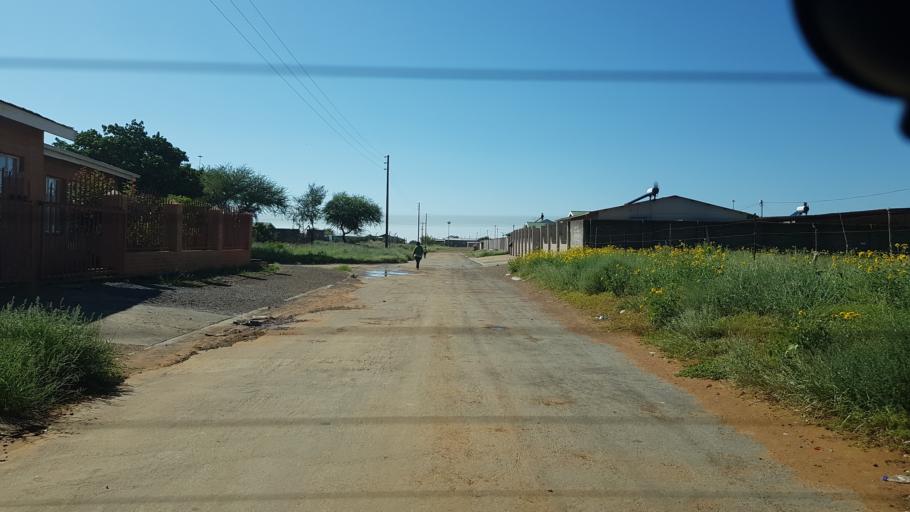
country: ZA
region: Northern Cape
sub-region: Siyanda District Municipality
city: Danielskuil
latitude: -28.1928
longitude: 23.5385
